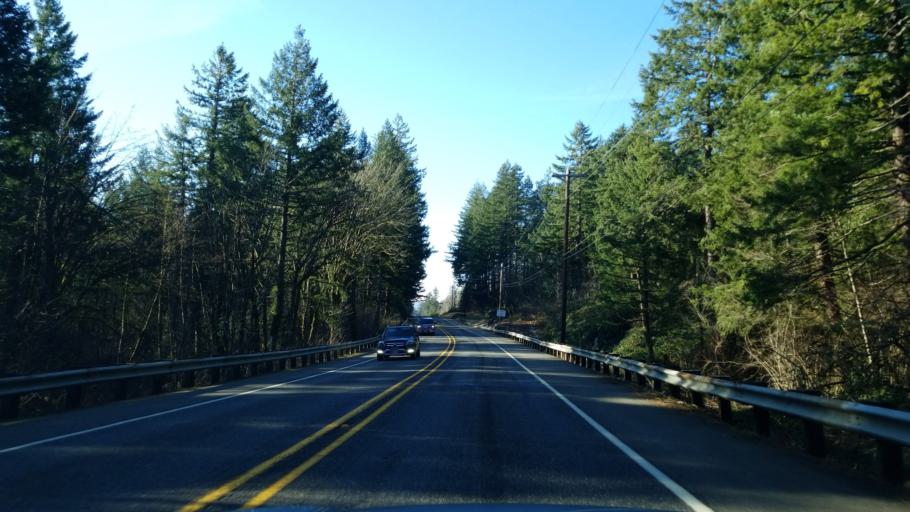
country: US
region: Washington
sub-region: Clark County
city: Washougal
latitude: 45.5975
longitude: -122.1277
